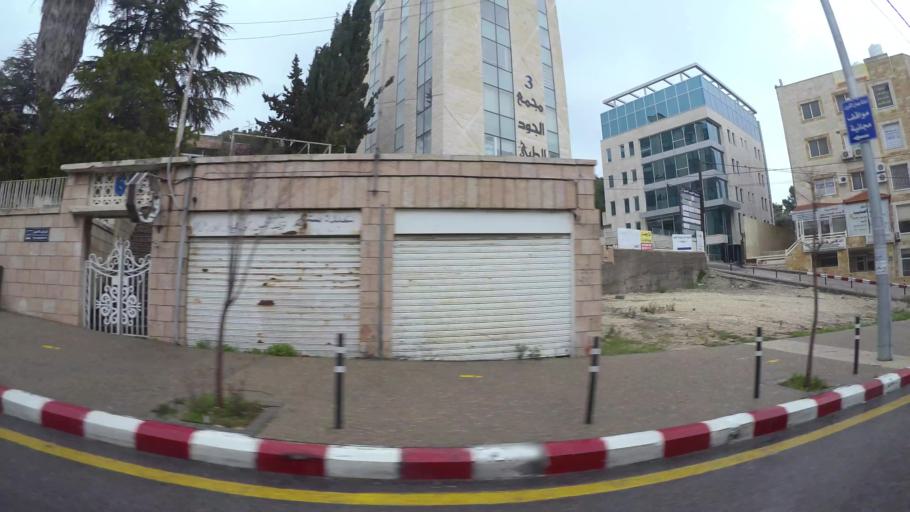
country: JO
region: Amman
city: Amman
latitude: 31.9528
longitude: 35.9001
